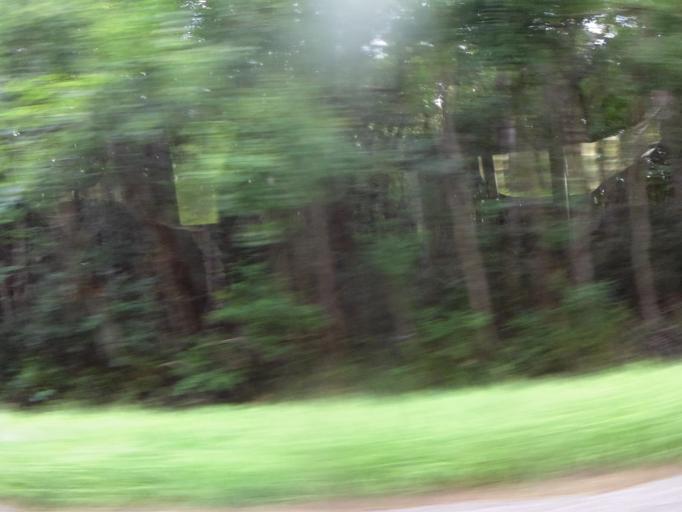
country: US
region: Florida
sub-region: Nassau County
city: Nassau Village-Ratliff
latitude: 30.3938
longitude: -81.7777
